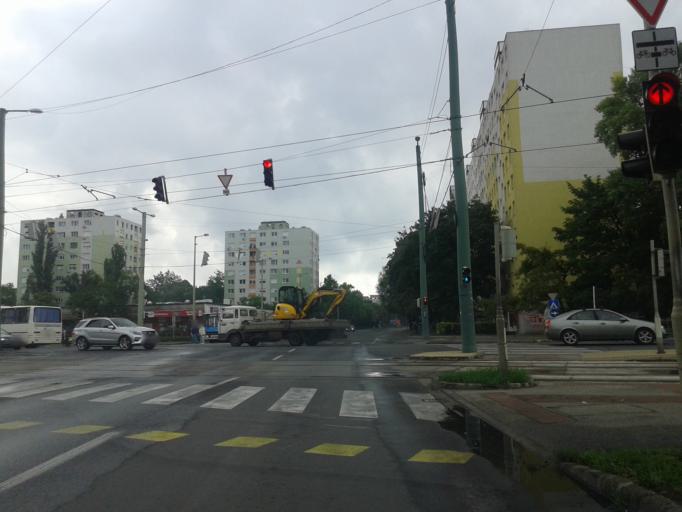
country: HU
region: Csongrad
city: Szeged
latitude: 46.2725
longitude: 20.1587
